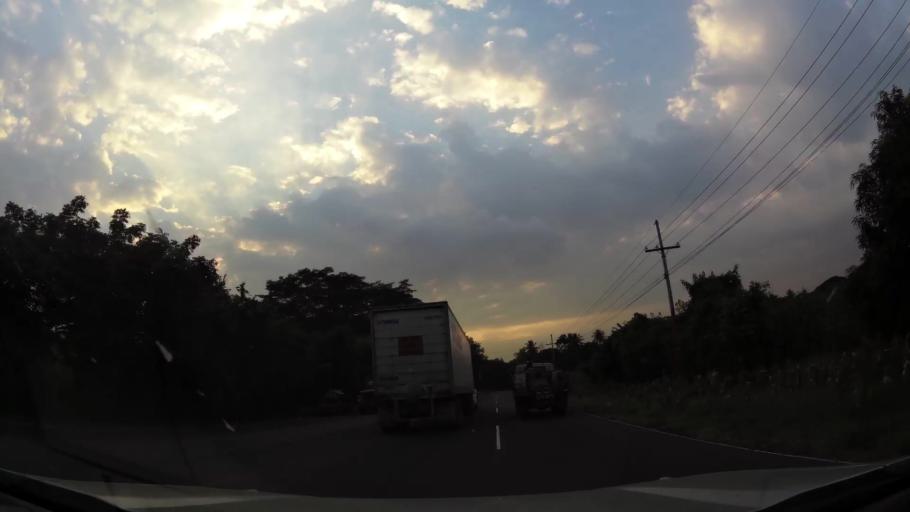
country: GT
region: Escuintla
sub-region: Municipio de La Democracia
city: La Democracia
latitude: 14.2669
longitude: -90.8910
